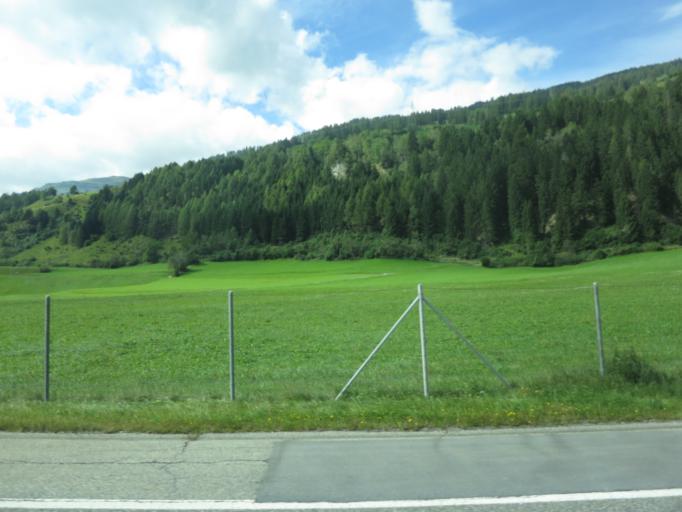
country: CH
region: Grisons
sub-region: Hinterrhein District
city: Thusis
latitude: 46.6387
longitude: 9.4407
